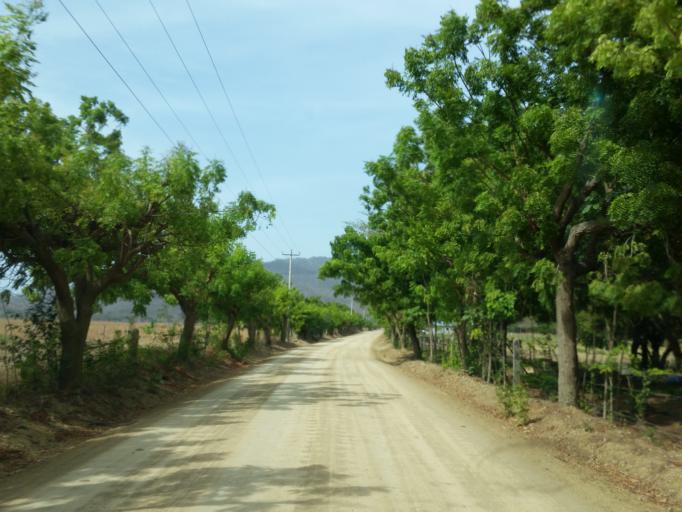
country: NI
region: Rivas
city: Tola
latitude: 11.4230
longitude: -86.0314
